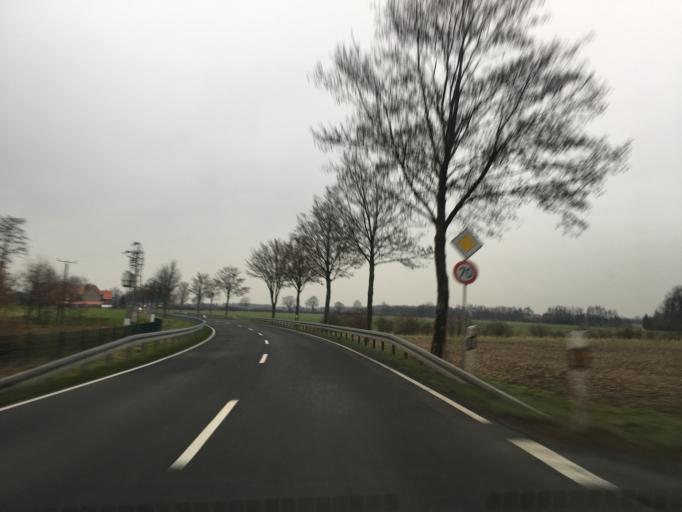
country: DE
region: North Rhine-Westphalia
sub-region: Regierungsbezirk Munster
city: Nordkirchen
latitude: 51.7779
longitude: 7.5458
